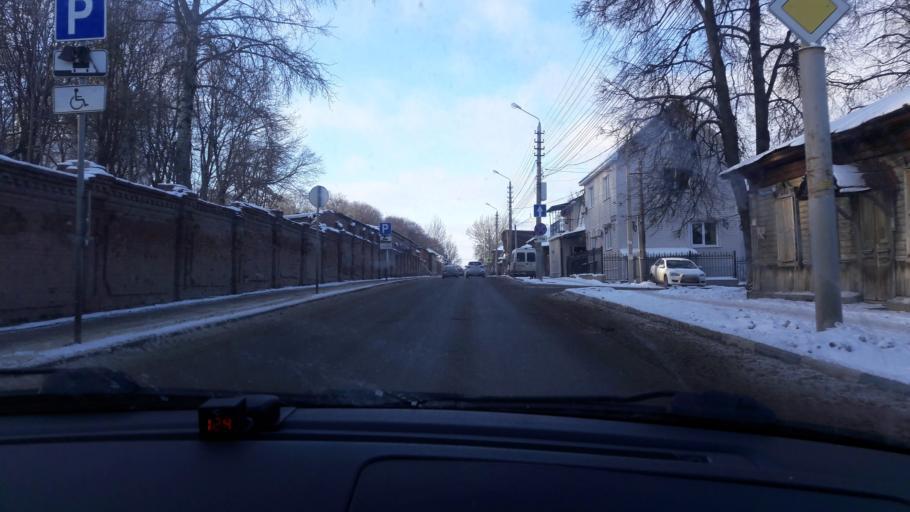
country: RU
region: Tula
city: Tula
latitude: 54.1807
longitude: 37.6152
